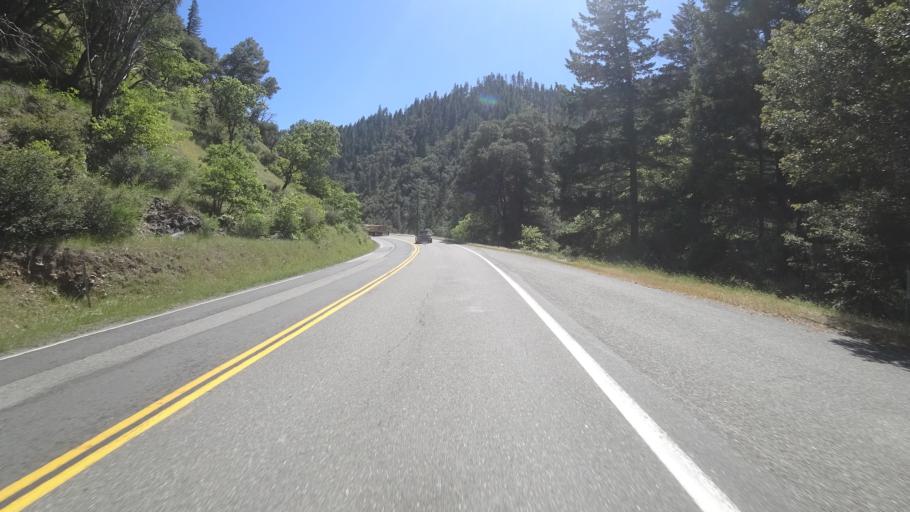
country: US
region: California
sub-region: Trinity County
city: Hayfork
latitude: 40.7547
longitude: -123.2838
